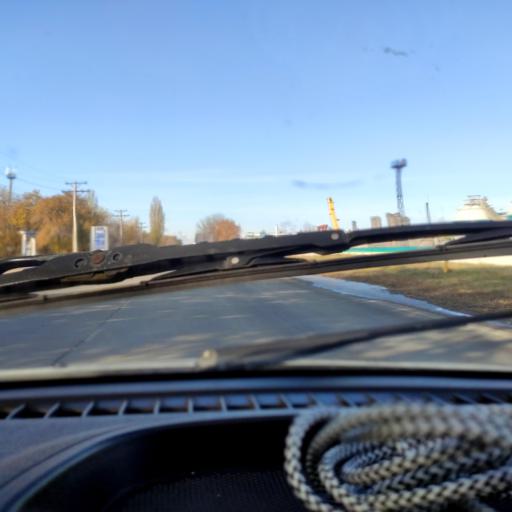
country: RU
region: Samara
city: Tol'yatti
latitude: 53.5321
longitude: 49.4567
